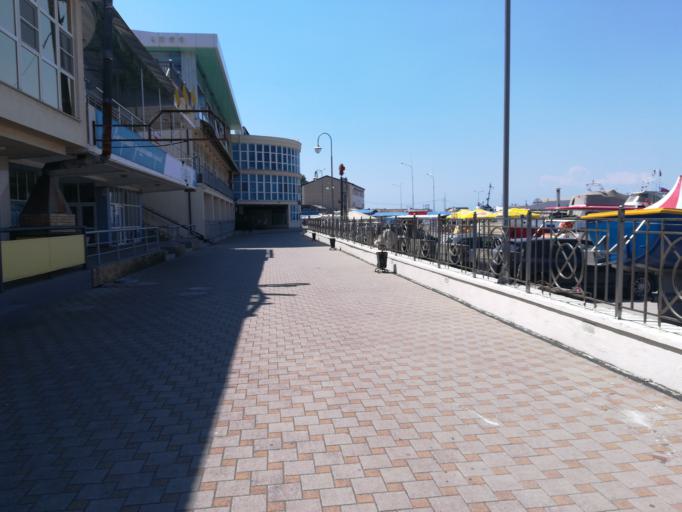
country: RU
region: Krasnodarskiy
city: Anapa
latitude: 44.8970
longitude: 37.3079
